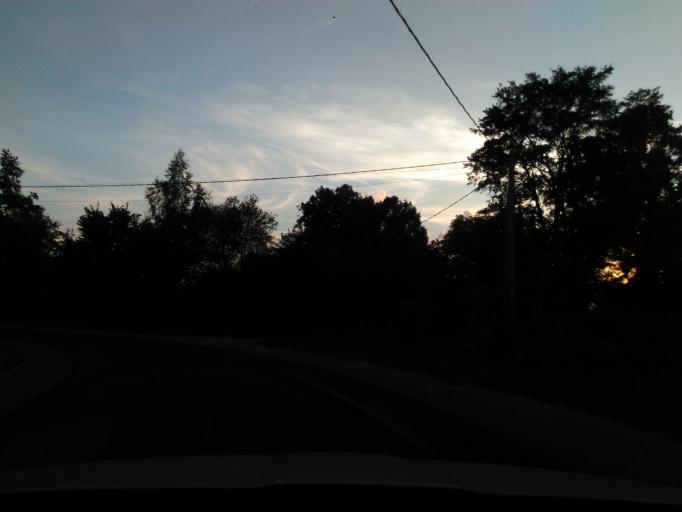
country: RU
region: Moskovskaya
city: Klin
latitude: 56.1632
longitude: 36.7718
